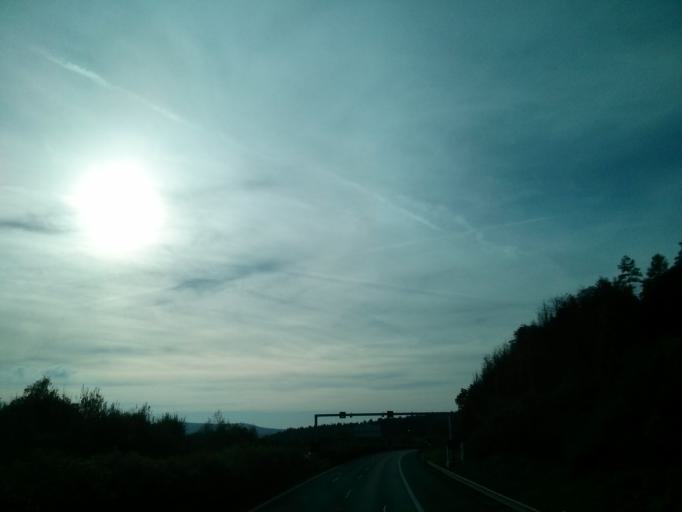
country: CZ
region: Plzensky
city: Stenovice
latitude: 49.6820
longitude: 13.4180
